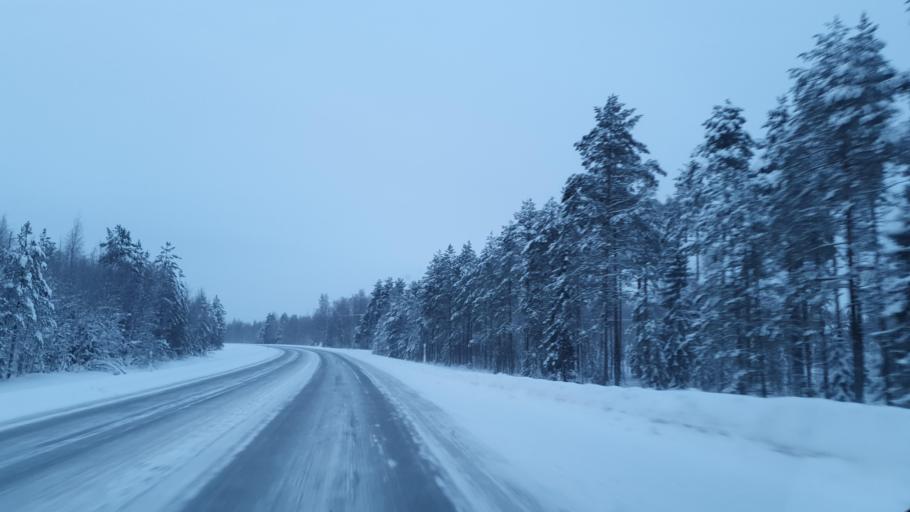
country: FI
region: Kainuu
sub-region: Kajaani
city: Vaala
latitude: 64.5928
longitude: 26.8017
